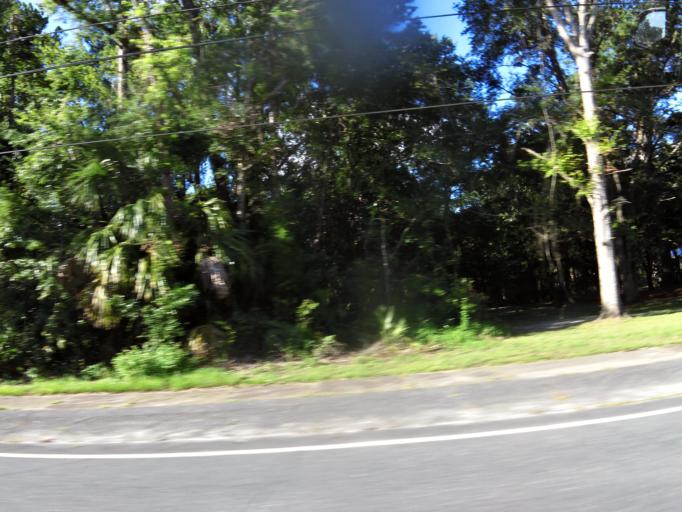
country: US
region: Florida
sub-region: Wakulla County
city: Crawfordville
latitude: 30.0619
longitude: -84.4952
